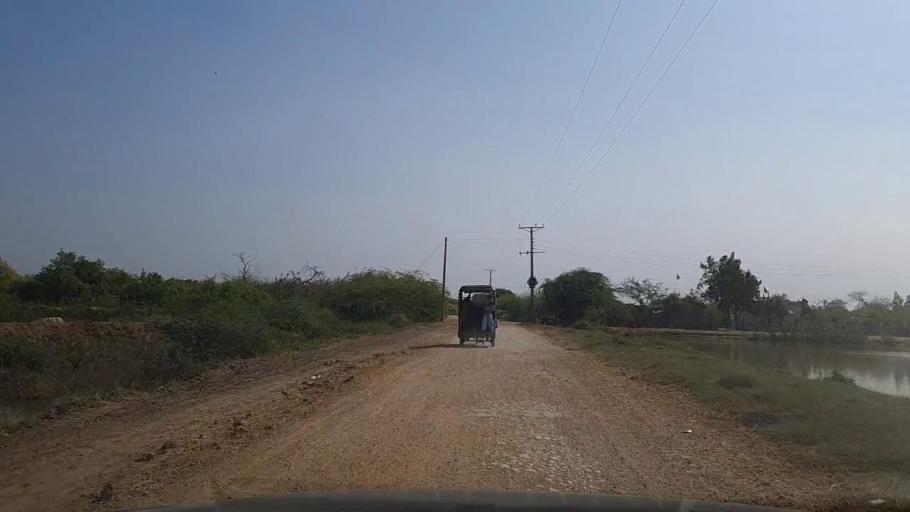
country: PK
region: Sindh
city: Thatta
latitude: 24.5826
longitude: 67.9133
